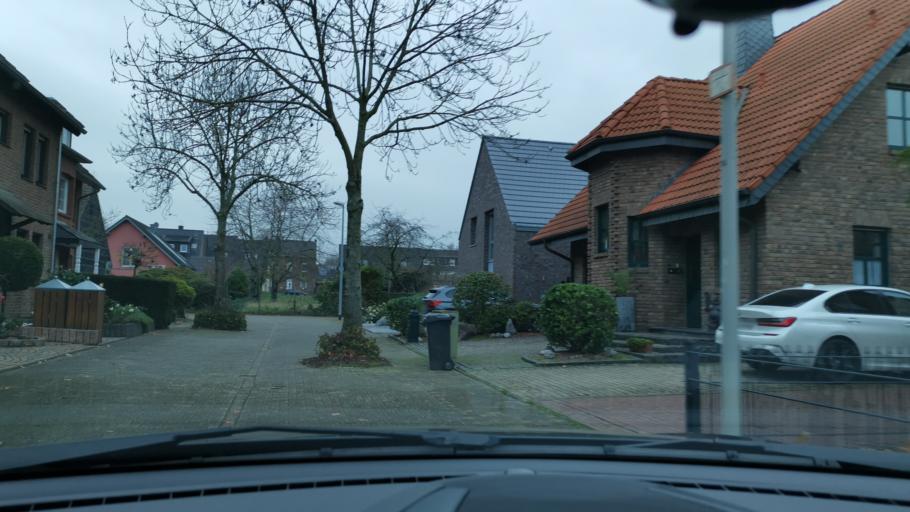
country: DE
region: North Rhine-Westphalia
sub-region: Regierungsbezirk Dusseldorf
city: Neubrueck
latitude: 51.1272
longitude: 6.6264
